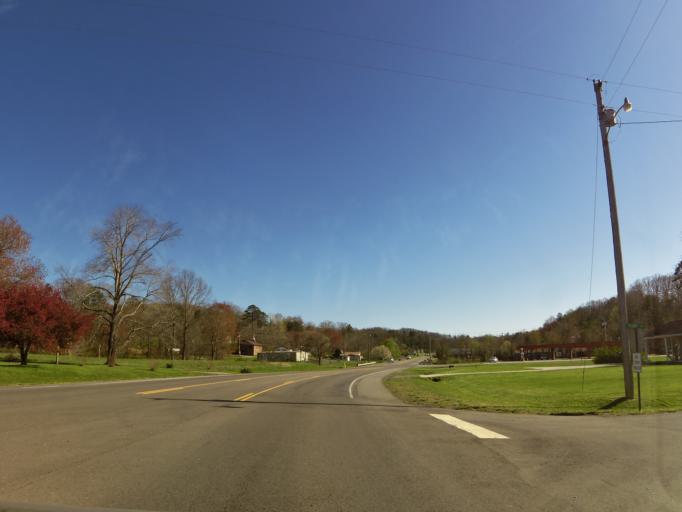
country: US
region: Tennessee
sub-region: Scott County
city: Oneida
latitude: 36.4950
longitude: -84.5066
